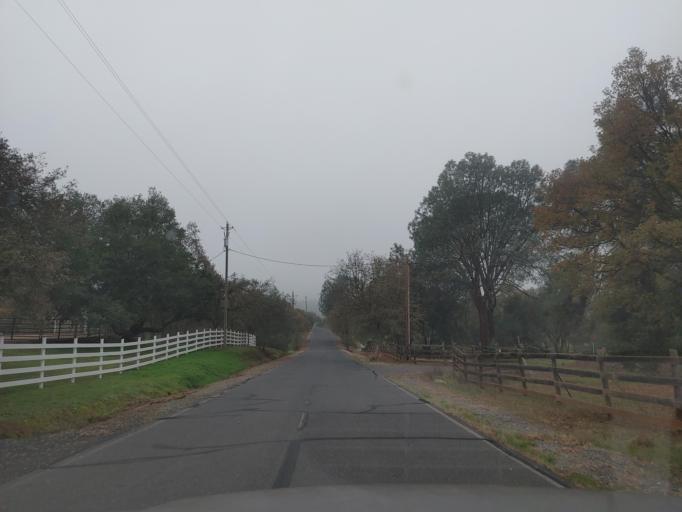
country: US
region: California
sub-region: Calaveras County
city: Copperopolis
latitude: 37.9411
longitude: -120.6139
